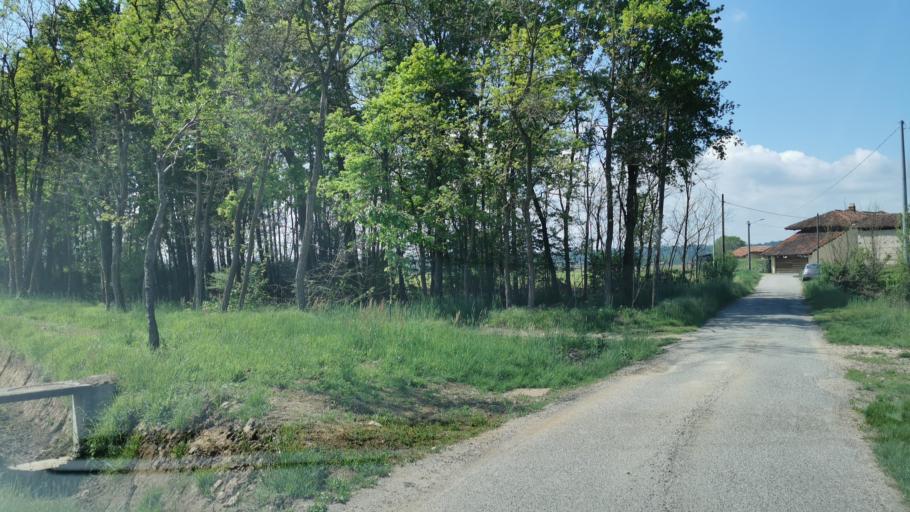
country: IT
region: Piedmont
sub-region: Provincia di Torino
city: Rivarossa
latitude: 45.2755
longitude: 7.7230
